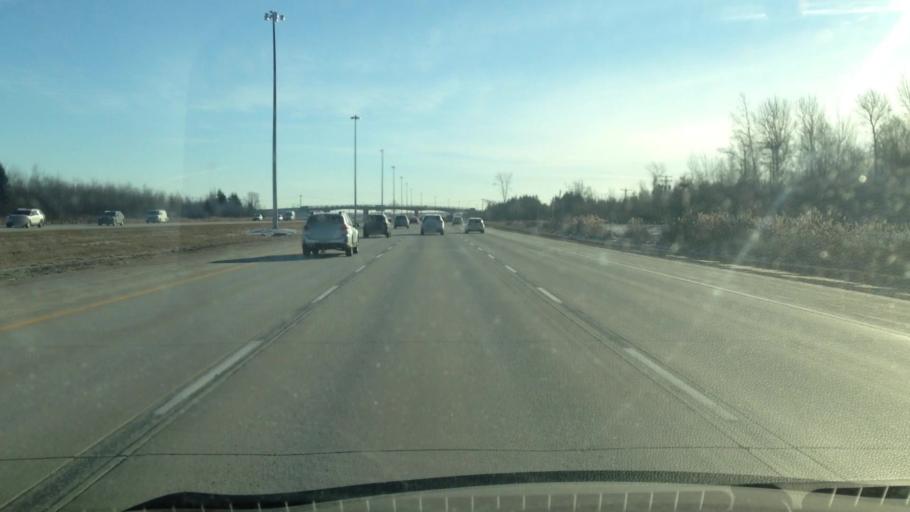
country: CA
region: Quebec
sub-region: Laurentides
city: Saint-Jerome
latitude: 45.7391
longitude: -73.9937
